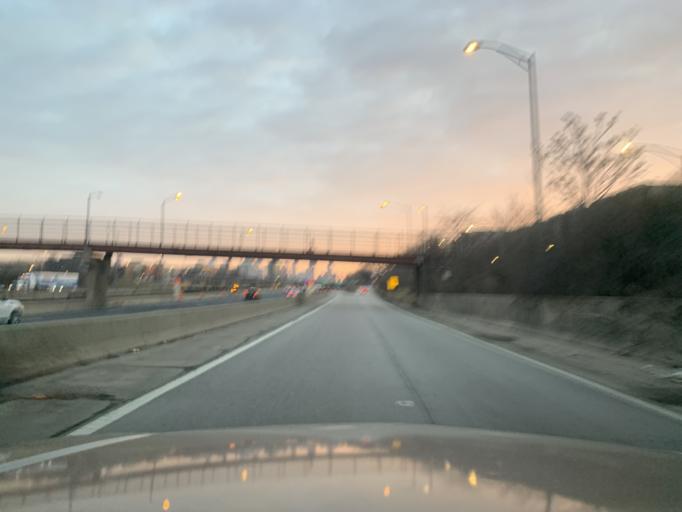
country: US
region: Illinois
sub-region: Cook County
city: Chicago
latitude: 41.8751
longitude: -87.6912
